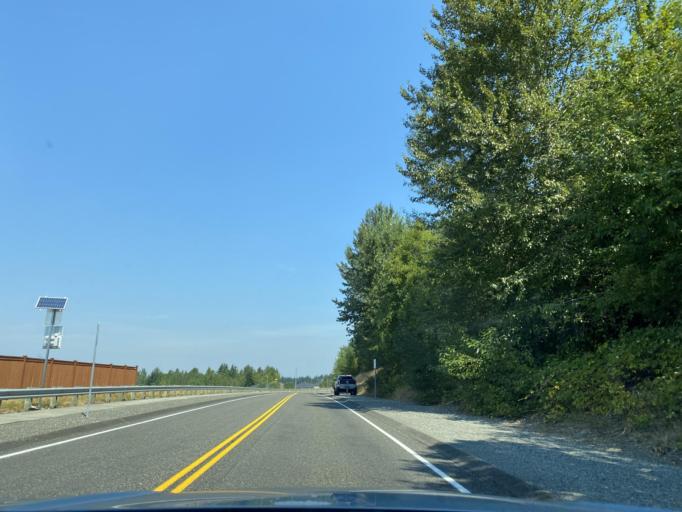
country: US
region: Washington
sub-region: Pierce County
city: Bonney Lake
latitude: 47.1657
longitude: -122.1918
